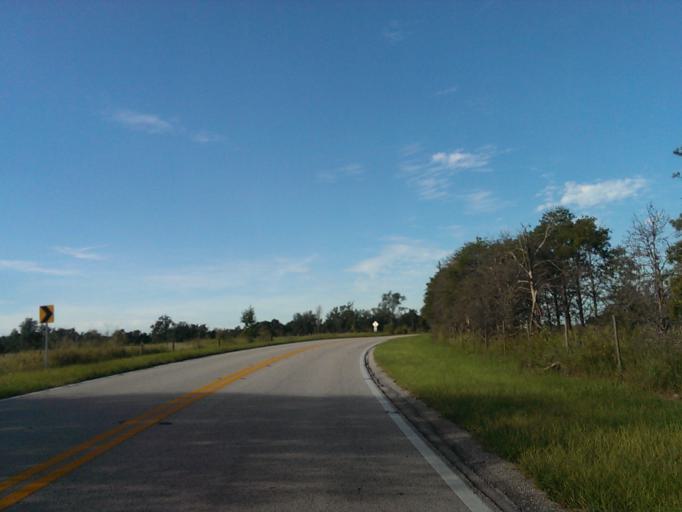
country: US
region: Florida
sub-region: Polk County
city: Citrus Ridge
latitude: 28.3897
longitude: -81.6360
